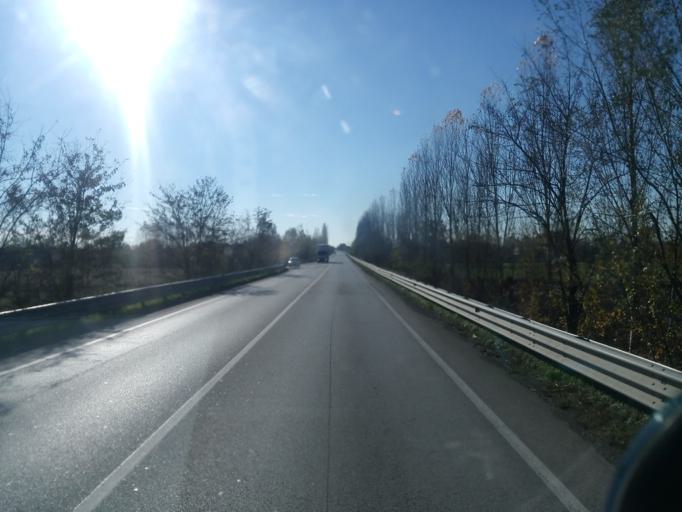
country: IT
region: Veneto
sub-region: Provincia di Padova
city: Camposampiero
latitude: 45.5703
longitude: 11.9544
